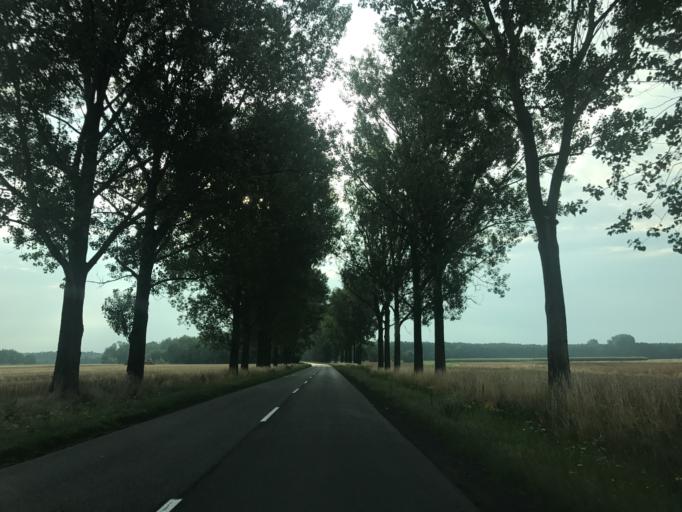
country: PL
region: Greater Poland Voivodeship
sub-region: Powiat rawicki
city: Rawicz
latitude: 51.6053
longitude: 16.9036
